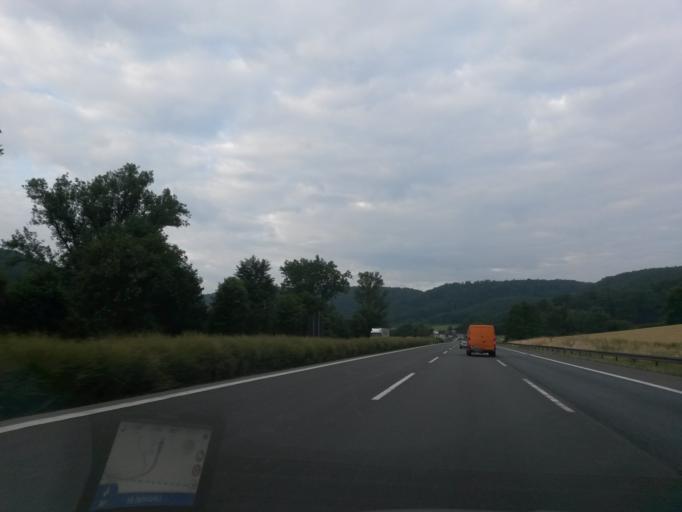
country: DE
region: Bavaria
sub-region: Regierungsbezirk Mittelfranken
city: Greding
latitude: 49.0182
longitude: 11.3629
